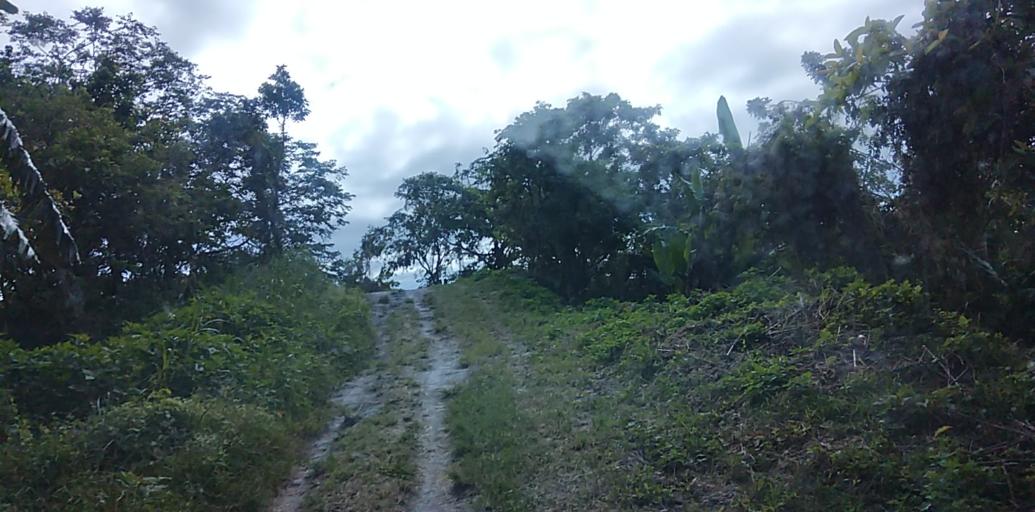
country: PH
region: Central Luzon
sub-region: Province of Pampanga
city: Babo-Pangulo
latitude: 15.1501
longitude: 120.4477
